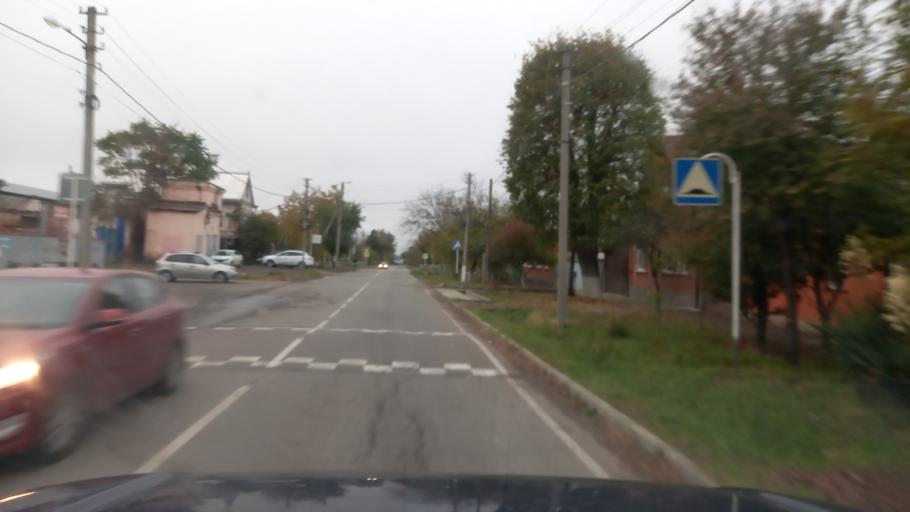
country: RU
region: Adygeya
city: Maykop
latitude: 44.6161
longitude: 40.1036
